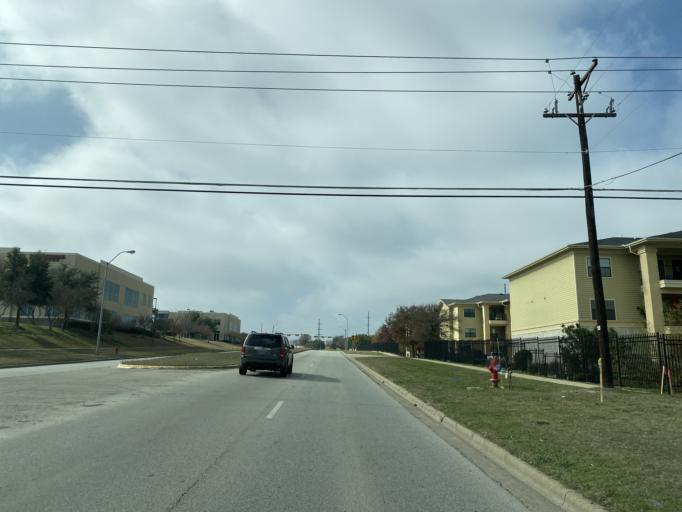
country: US
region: Texas
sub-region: Williamson County
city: Round Rock
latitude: 30.5366
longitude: -97.6793
